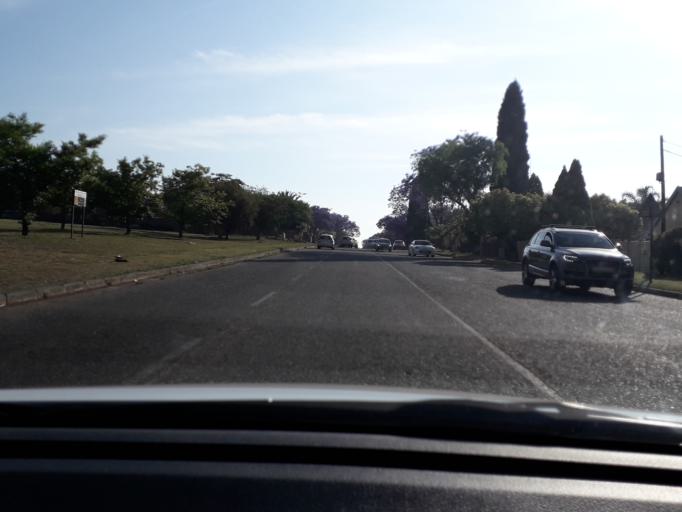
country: ZA
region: Gauteng
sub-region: West Rand District Municipality
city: Muldersdriseloop
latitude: -26.0724
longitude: 27.9412
